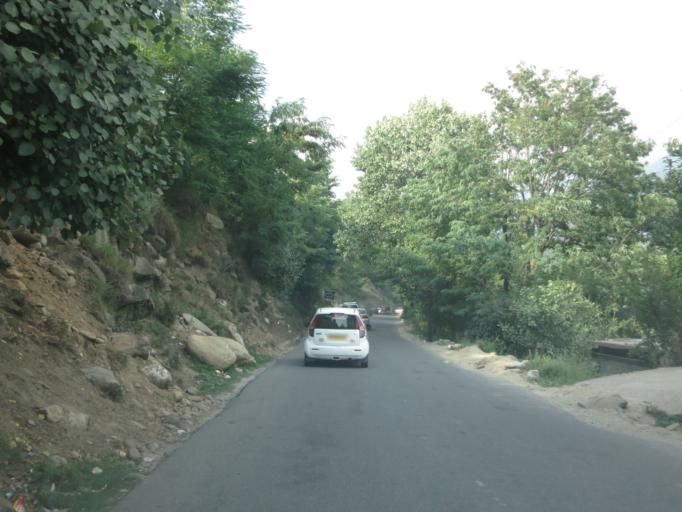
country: IN
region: Himachal Pradesh
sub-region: Kulu
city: Nagar
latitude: 32.1104
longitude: 77.1444
